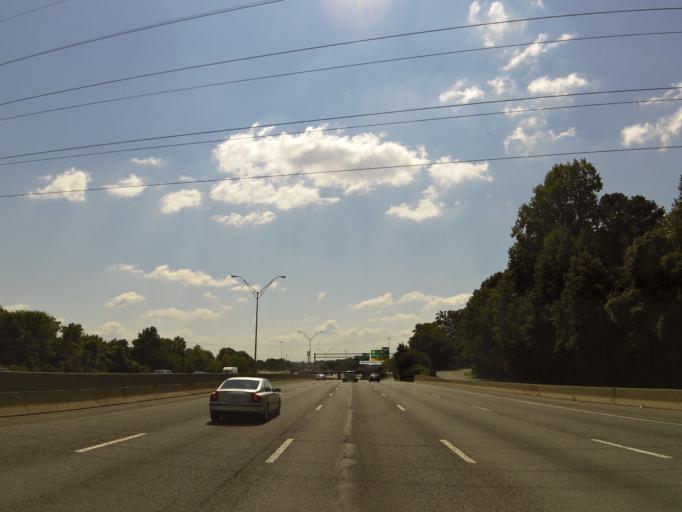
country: US
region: North Carolina
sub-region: Mecklenburg County
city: Charlotte
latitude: 35.2654
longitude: -80.8752
